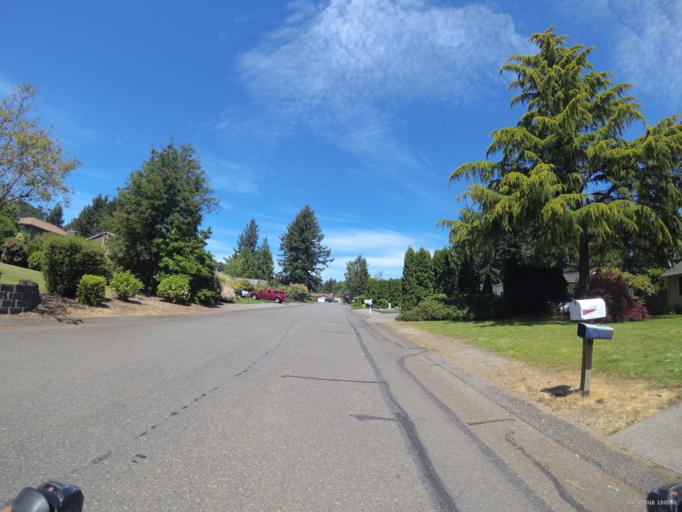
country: US
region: Washington
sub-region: Pierce County
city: University Place
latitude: 47.2028
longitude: -122.5666
